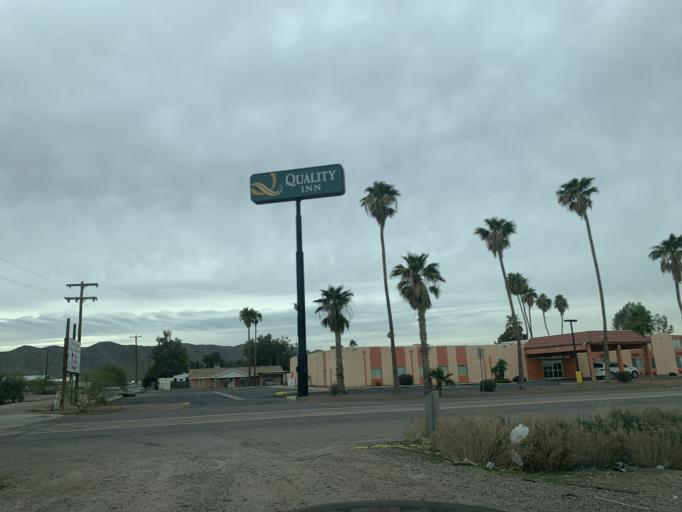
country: US
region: Arizona
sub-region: Pinal County
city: Arizona City
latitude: 32.8142
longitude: -111.6708
